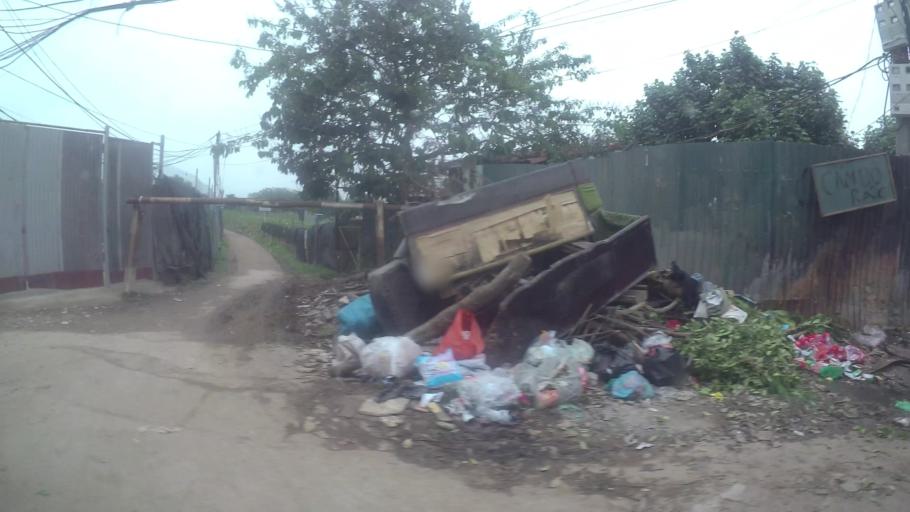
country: VN
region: Ha Noi
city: Tay Ho
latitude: 21.0611
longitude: 105.8388
